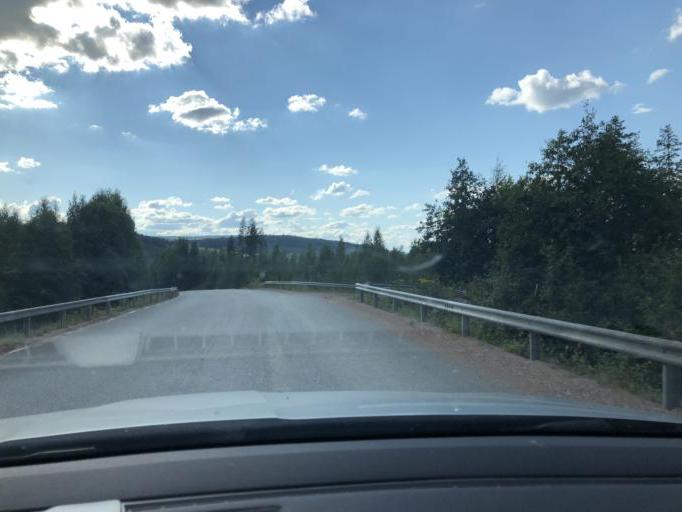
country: SE
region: Vaesternorrland
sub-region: Solleftea Kommun
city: Solleftea
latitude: 63.3148
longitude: 17.2111
